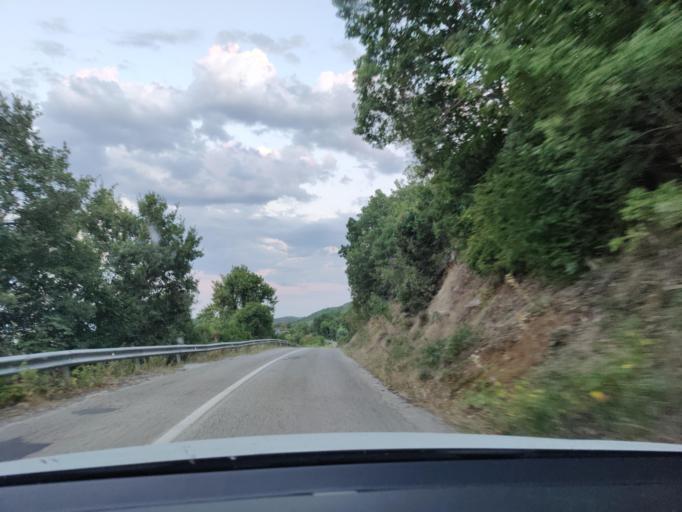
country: GR
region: Central Macedonia
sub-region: Nomos Serron
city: Chrysochorafa
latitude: 41.1690
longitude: 23.1780
